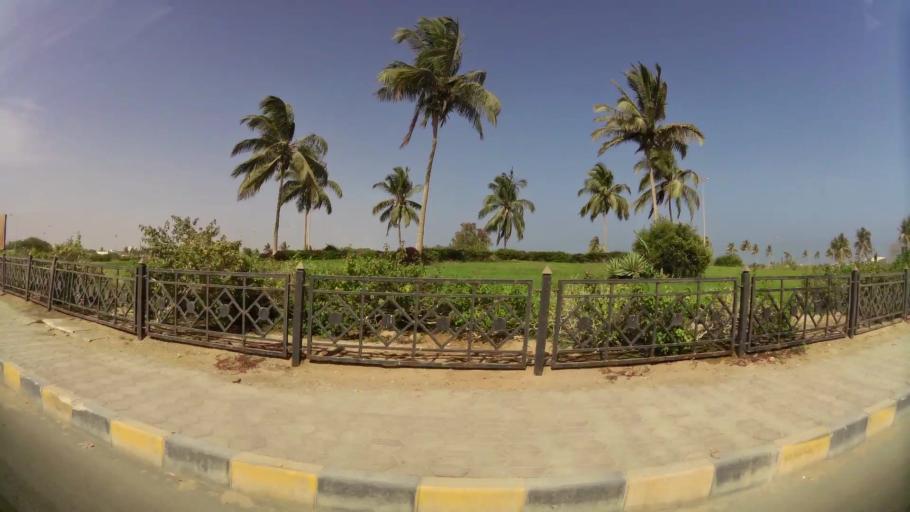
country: OM
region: Zufar
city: Salalah
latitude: 16.9847
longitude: 54.0169
